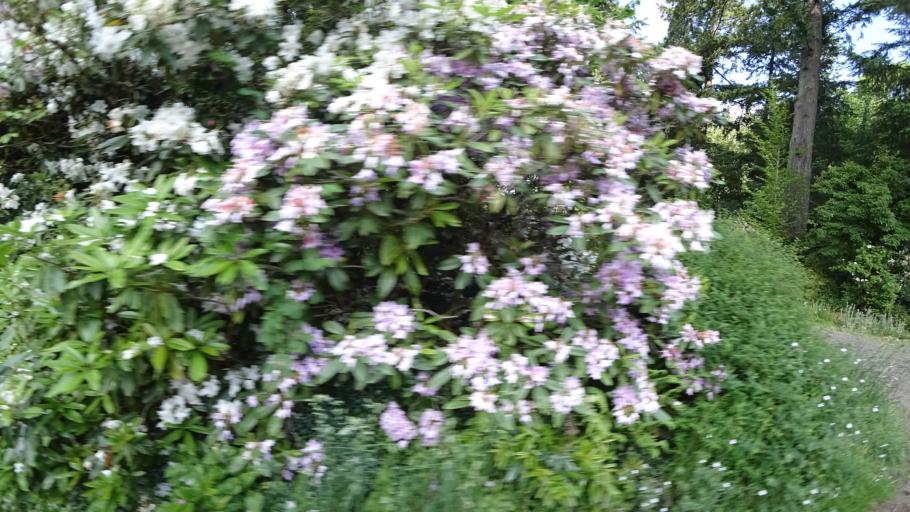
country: US
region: Oregon
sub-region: Washington County
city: West Slope
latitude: 45.5013
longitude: -122.7286
